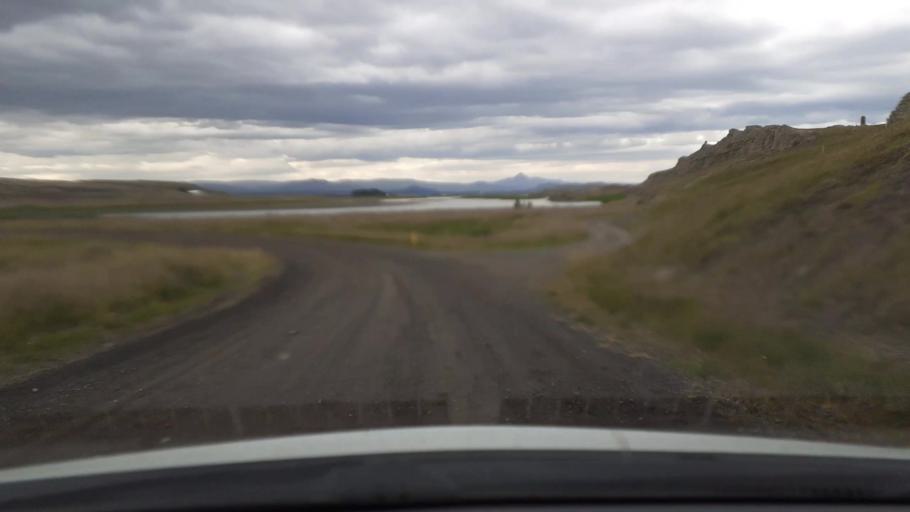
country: IS
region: West
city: Borgarnes
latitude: 64.6024
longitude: -21.6970
